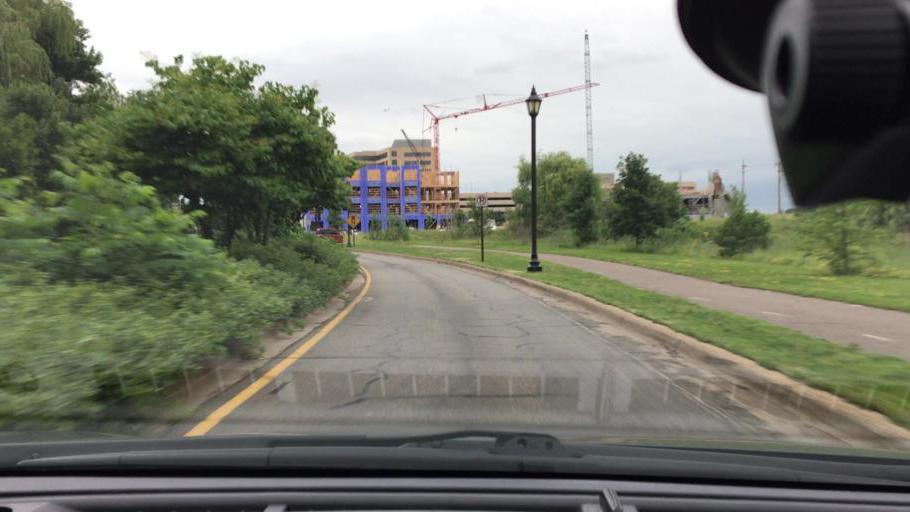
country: US
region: Minnesota
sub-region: Hennepin County
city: Saint Louis Park
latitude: 44.9762
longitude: -93.3527
